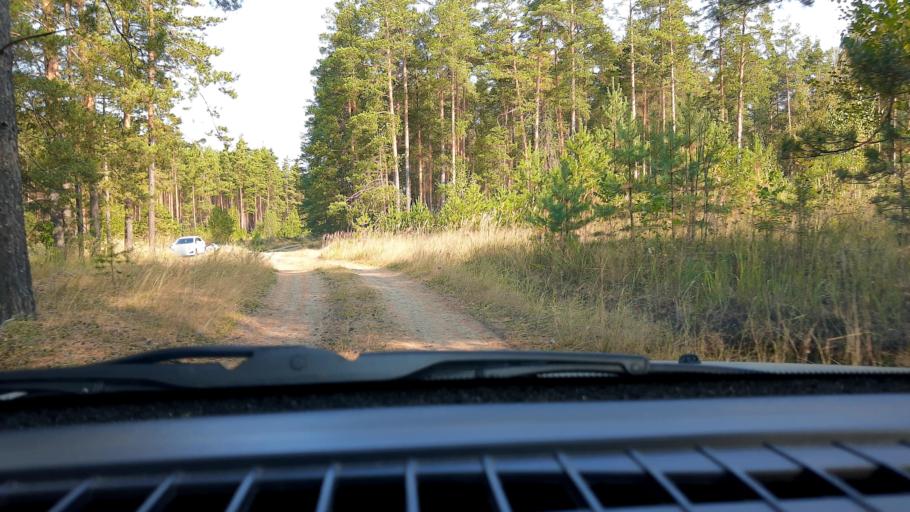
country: RU
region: Nizjnij Novgorod
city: Lukino
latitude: 56.3991
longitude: 43.6420
